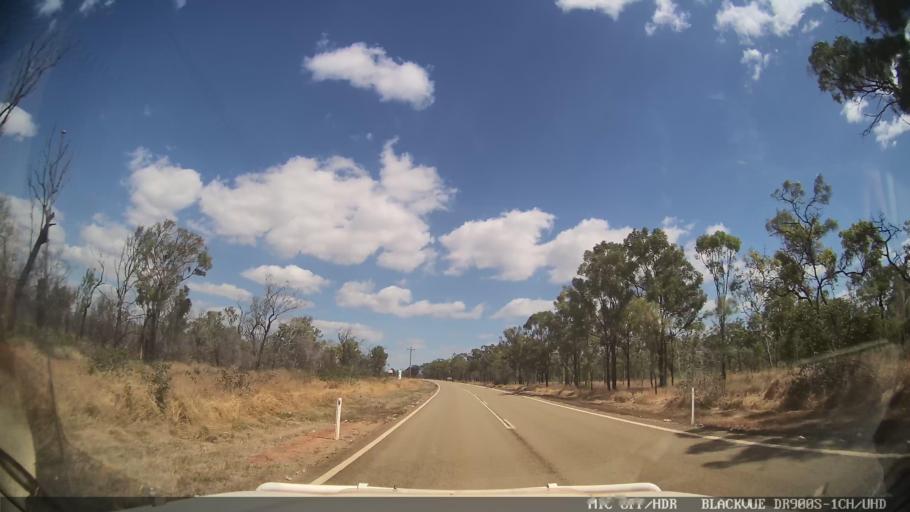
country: AU
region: Queensland
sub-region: Tablelands
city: Ravenshoe
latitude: -18.1340
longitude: 144.8139
